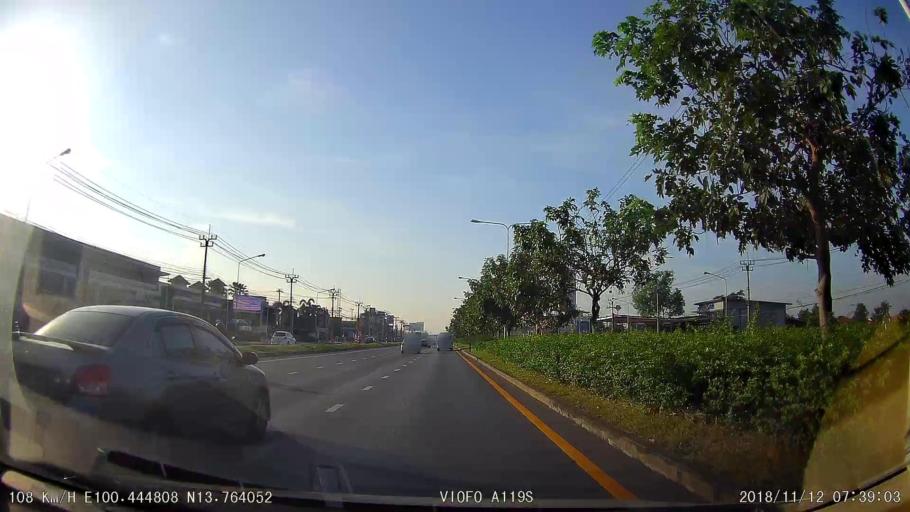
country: TH
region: Bangkok
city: Taling Chan
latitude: 13.7628
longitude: 100.4449
